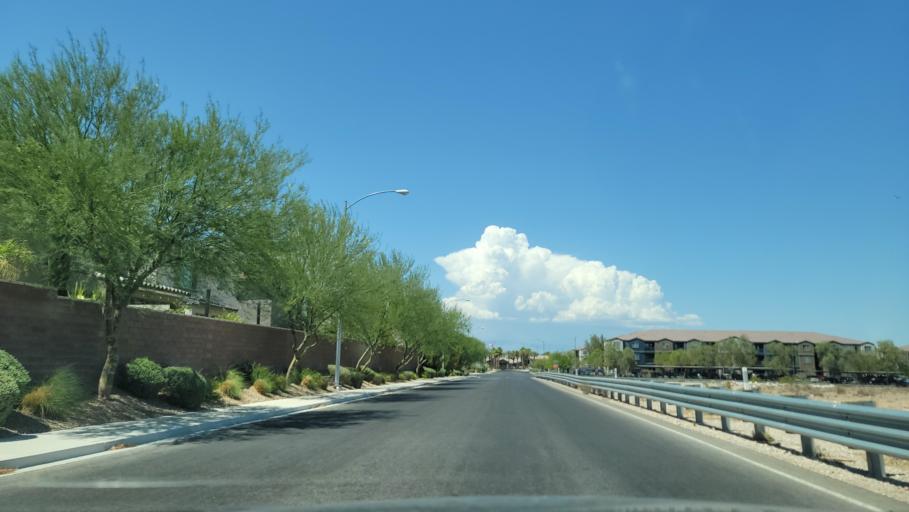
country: US
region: Nevada
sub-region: Clark County
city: Enterprise
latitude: 36.0578
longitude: -115.2656
